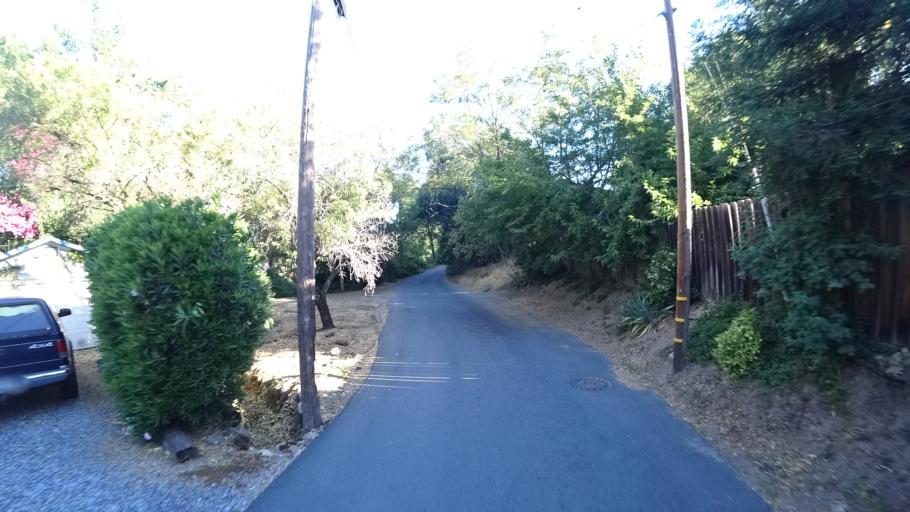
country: US
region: California
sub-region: Amador County
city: Jackson
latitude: 38.3011
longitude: -120.7072
